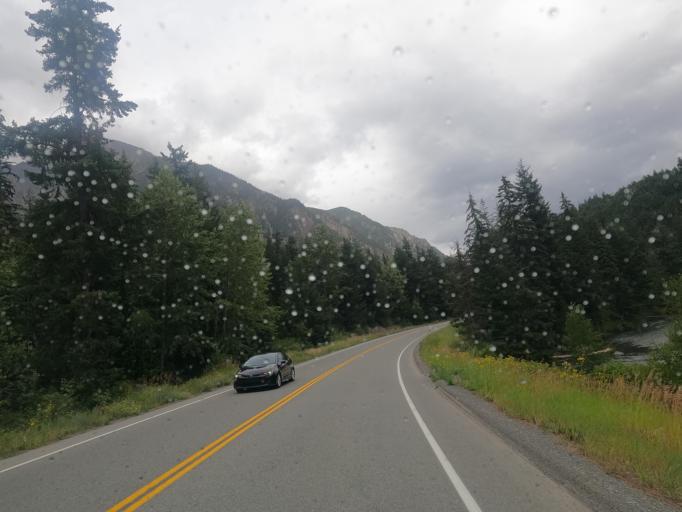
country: CA
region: British Columbia
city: Lillooet
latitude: 50.5278
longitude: -122.1603
